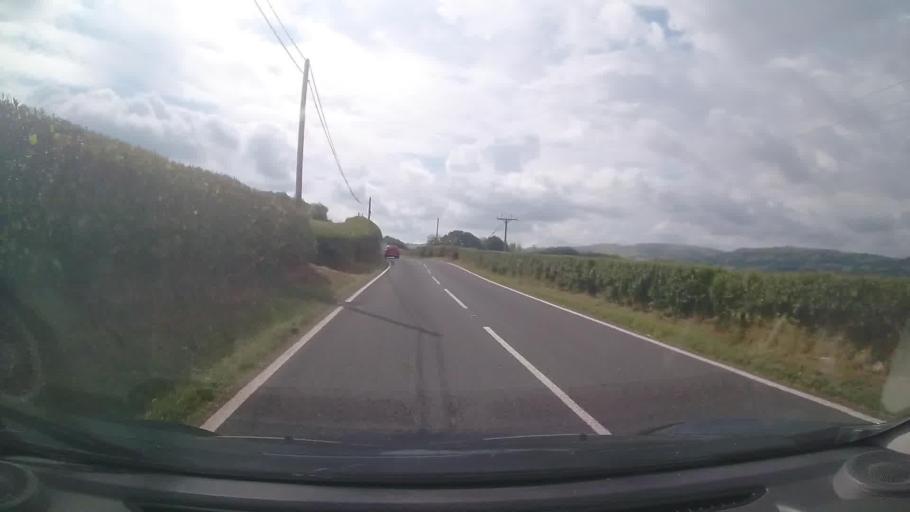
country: GB
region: Wales
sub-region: Sir Powys
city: Mochdre
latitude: 52.4925
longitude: -3.3428
